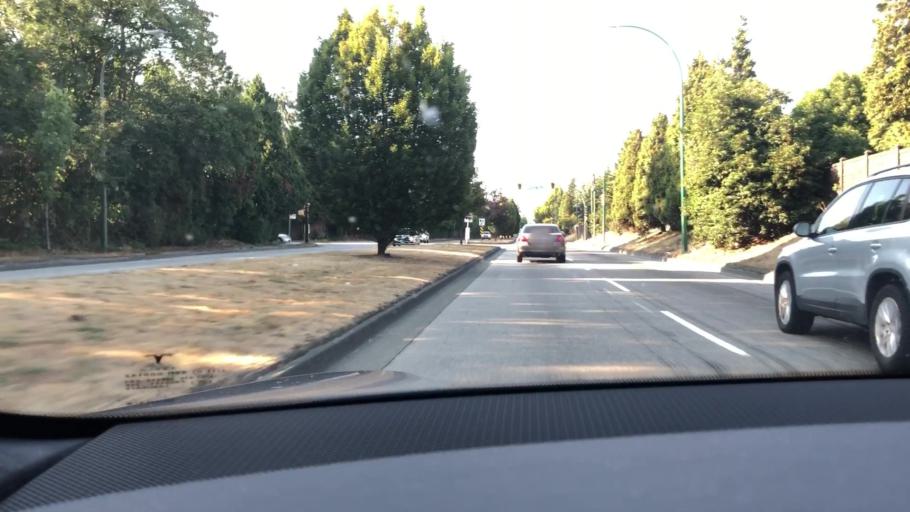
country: CA
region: British Columbia
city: Burnaby
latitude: 49.2168
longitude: -123.0237
